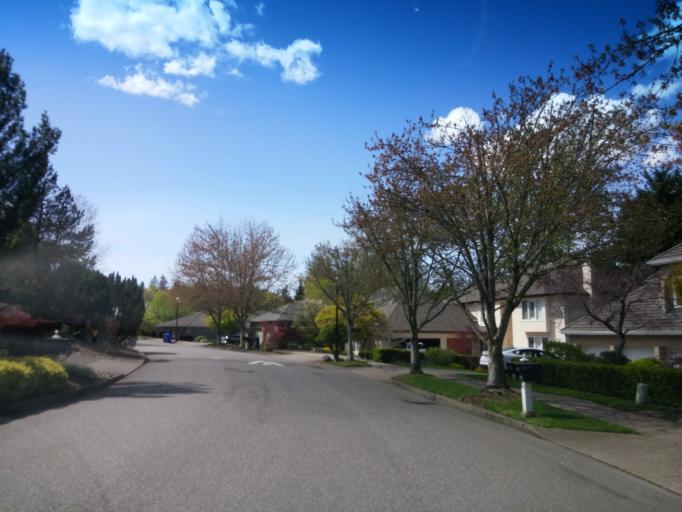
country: US
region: Oregon
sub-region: Washington County
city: West Haven
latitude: 45.5359
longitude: -122.7802
